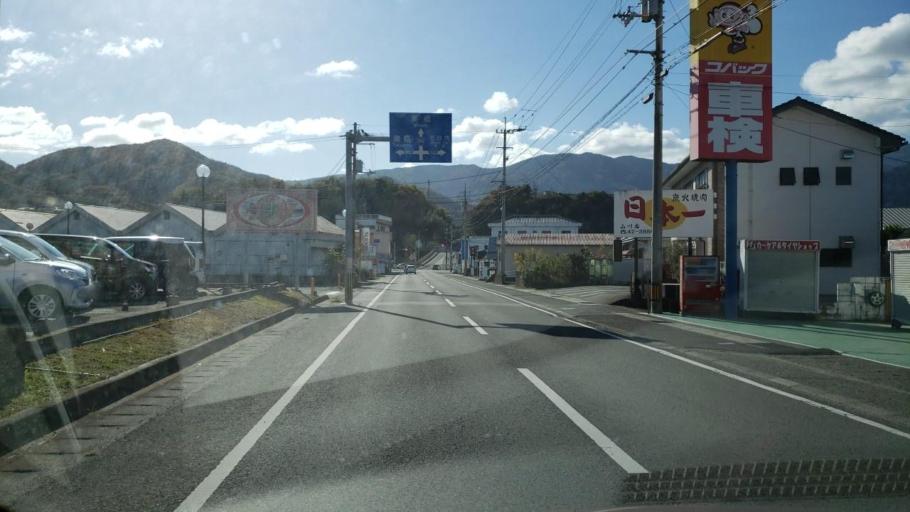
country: JP
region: Tokushima
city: Wakimachi
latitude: 34.0587
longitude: 134.2384
